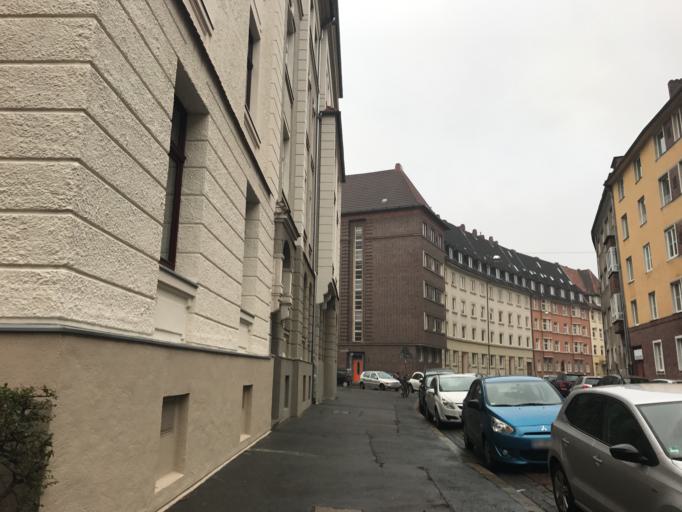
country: DE
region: Lower Saxony
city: Hannover
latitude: 52.3637
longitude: 9.7591
